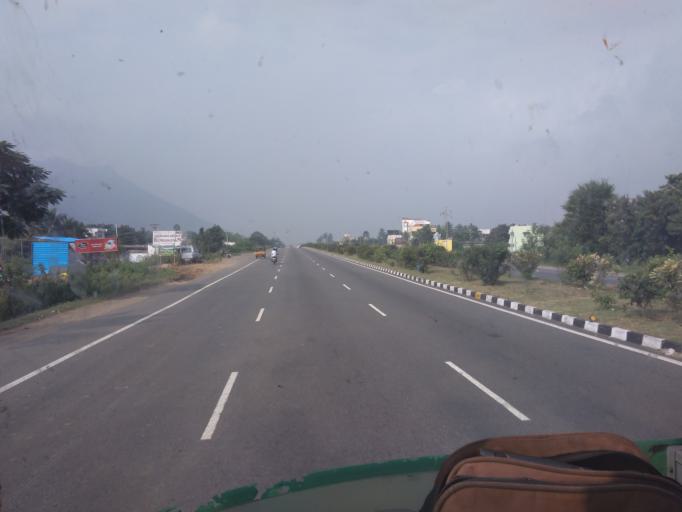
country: IN
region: Tamil Nadu
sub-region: Vellore
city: Pallikondai
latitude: 12.9095
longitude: 78.9773
